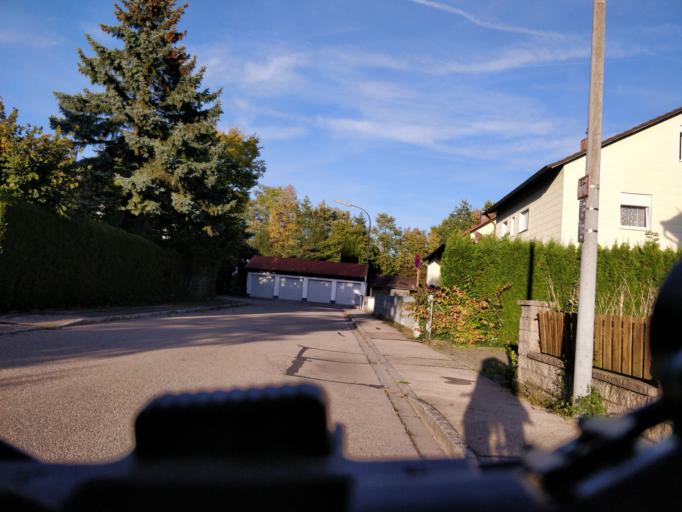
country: DE
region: Bavaria
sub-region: Swabia
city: Mering
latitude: 48.2789
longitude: 10.9732
